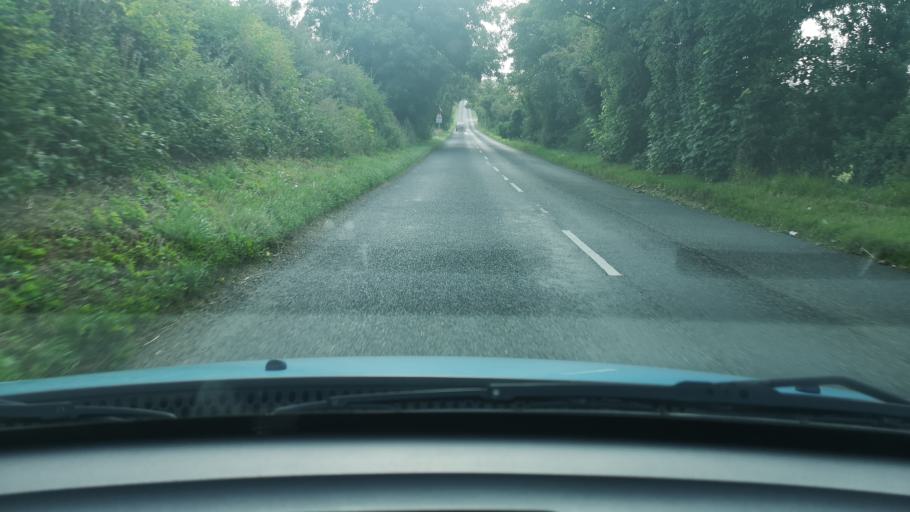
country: GB
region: England
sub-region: Doncaster
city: Campsall
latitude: 53.6175
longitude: -1.2000
